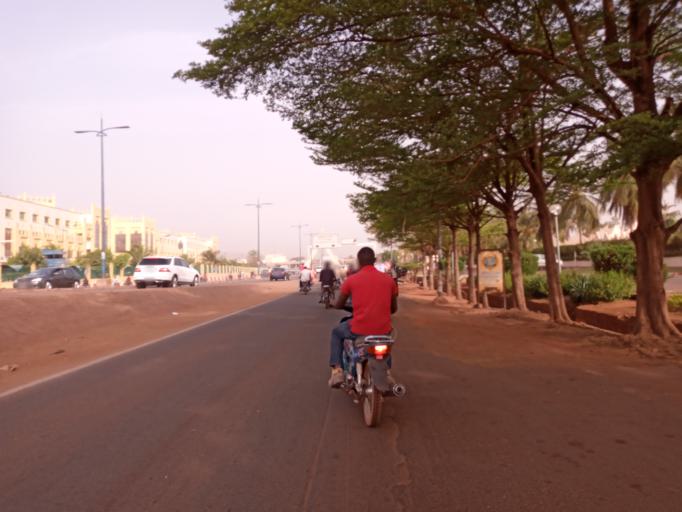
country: ML
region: Bamako
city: Bamako
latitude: 12.6294
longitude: -8.0088
